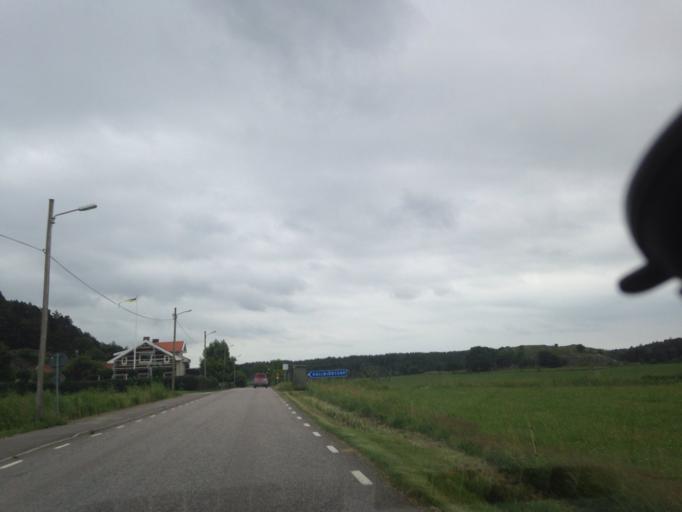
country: SE
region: Vaestra Goetaland
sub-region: Kungalvs Kommun
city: Kode
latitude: 57.8414
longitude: 11.7936
